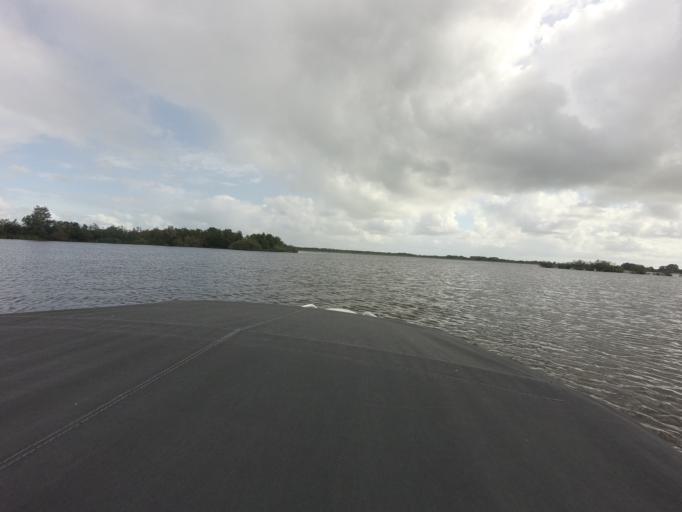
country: NL
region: Friesland
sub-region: Gemeente Boarnsterhim
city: Warten
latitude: 53.1162
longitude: 5.9277
